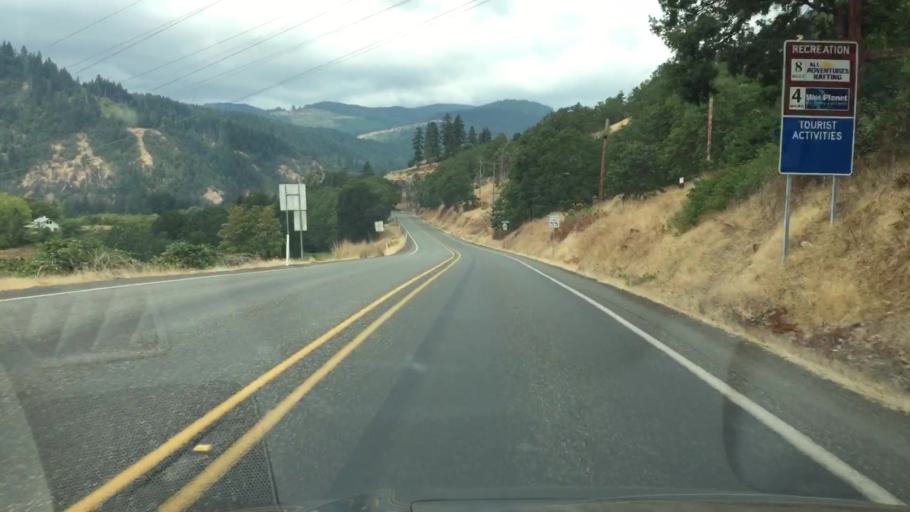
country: US
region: Washington
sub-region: Klickitat County
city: White Salmon
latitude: 45.7575
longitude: -121.5204
